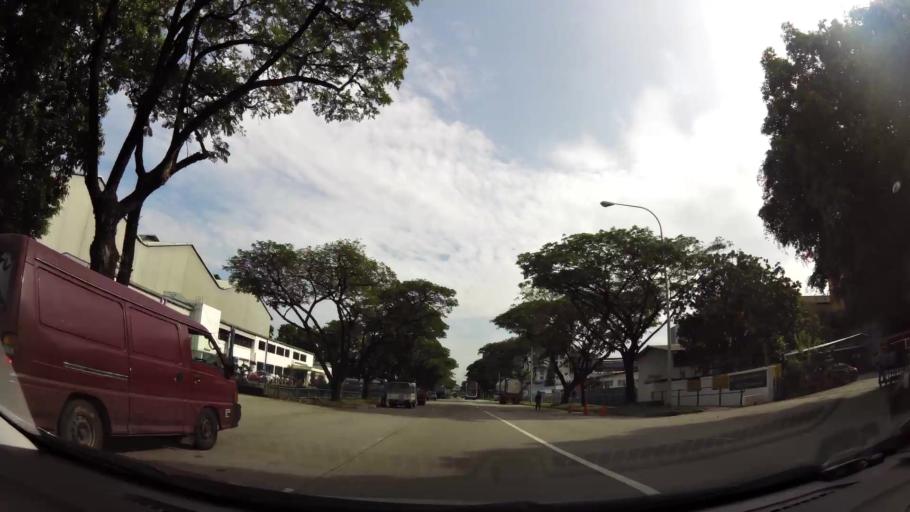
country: MY
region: Johor
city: Johor Bahru
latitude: 1.3100
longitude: 103.6517
